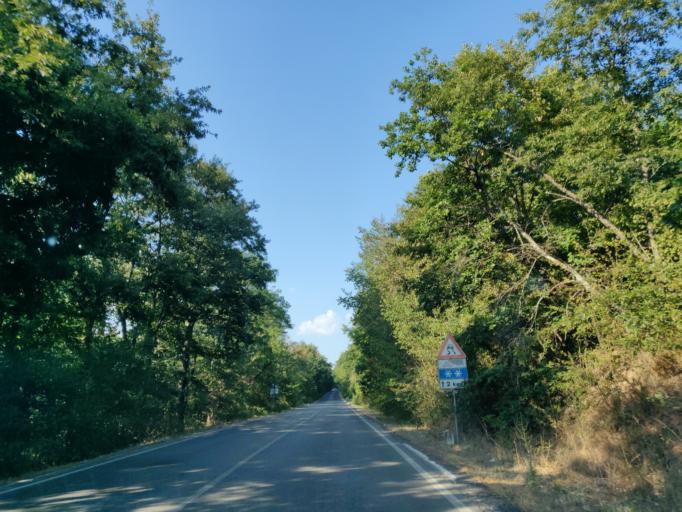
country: IT
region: Latium
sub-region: Provincia di Viterbo
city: Valentano
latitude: 42.5957
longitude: 11.8384
